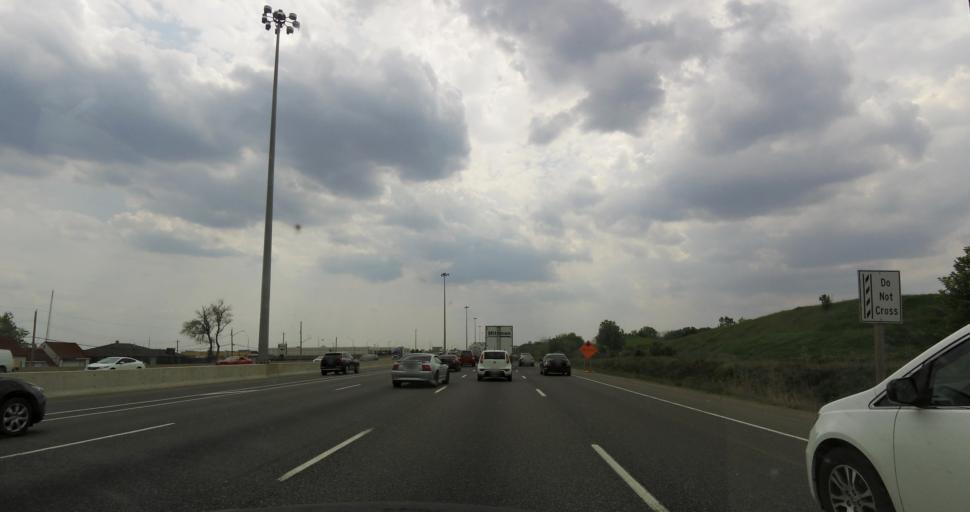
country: CA
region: Ontario
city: Oakville
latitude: 43.4044
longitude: -79.7468
